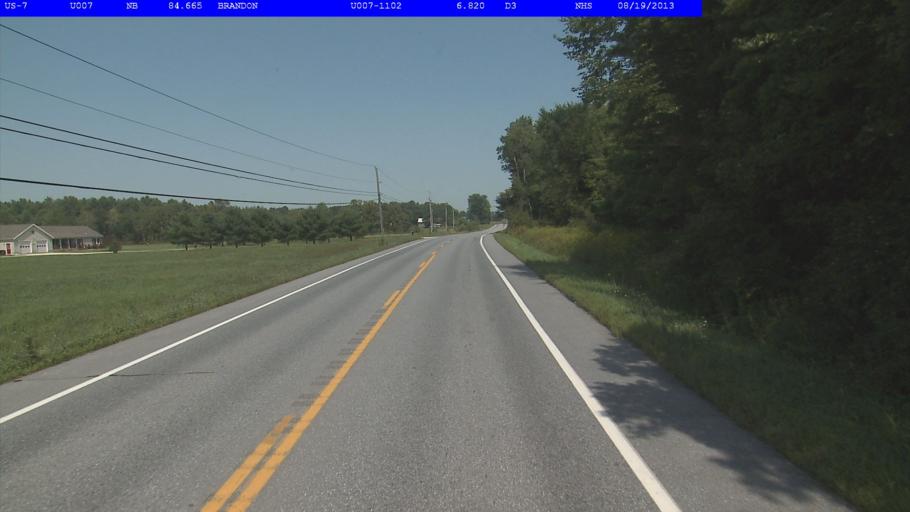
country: US
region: Vermont
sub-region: Rutland County
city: Brandon
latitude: 43.8345
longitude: -73.1059
